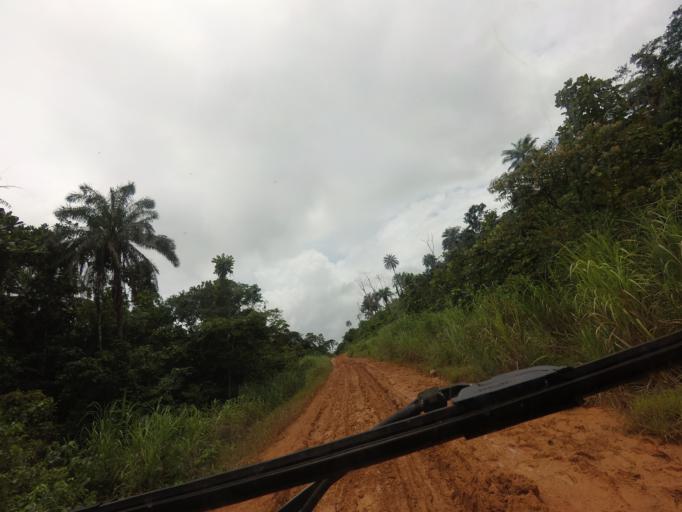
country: SL
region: Eastern Province
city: Tombodu
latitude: 8.1555
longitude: -10.6558
